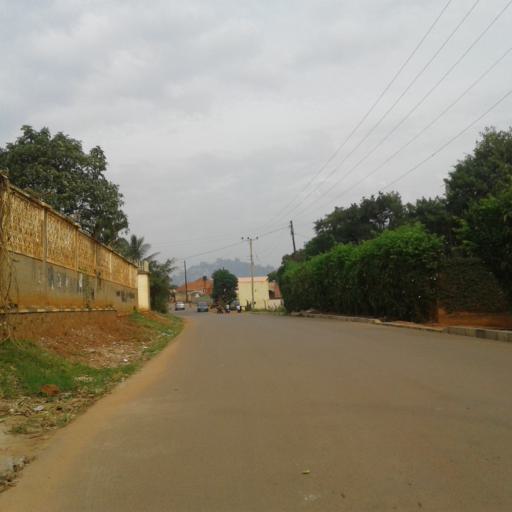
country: UG
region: Central Region
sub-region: Kampala District
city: Kampala
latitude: 0.2751
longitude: 32.6267
